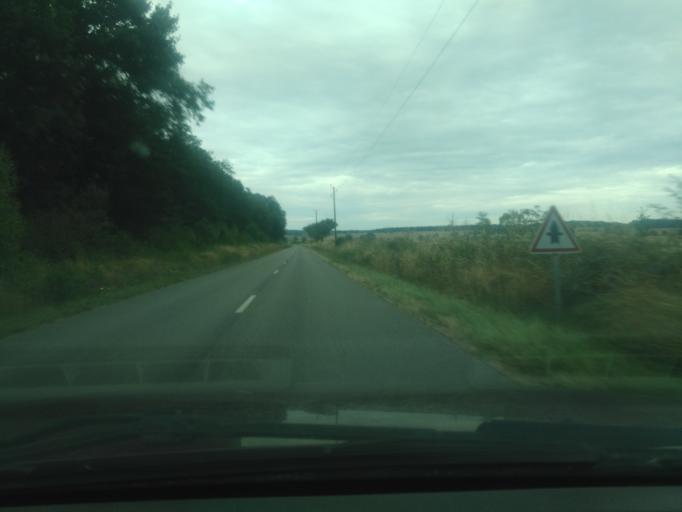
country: FR
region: Bourgogne
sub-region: Departement de la Nievre
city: Dornes
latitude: 46.7729
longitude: 3.3572
